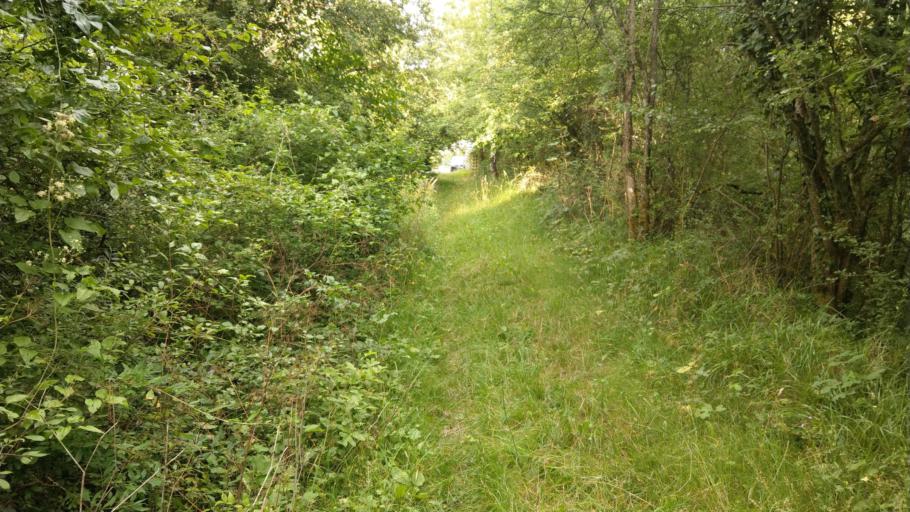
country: BE
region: Wallonia
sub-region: Province de Namur
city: Couvin
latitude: 50.0714
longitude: 4.4647
